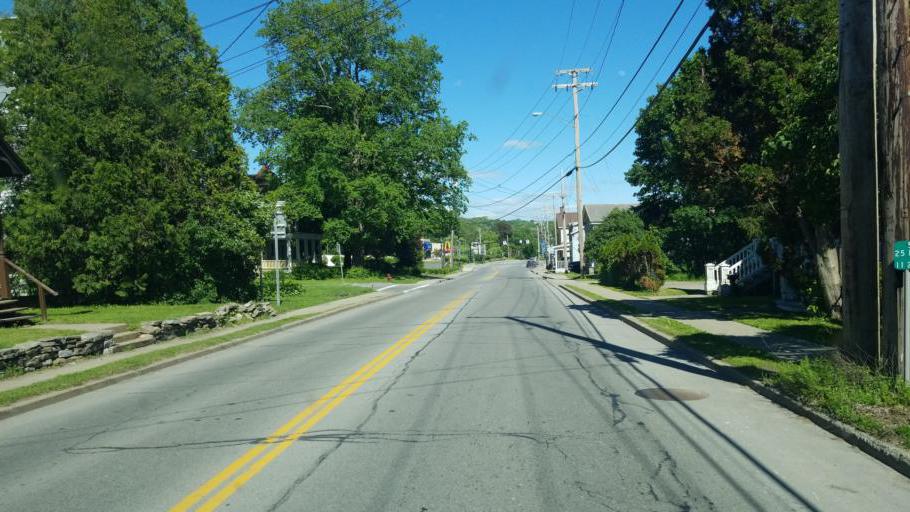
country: US
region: New York
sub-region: Montgomery County
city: Canajoharie
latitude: 42.9111
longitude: -74.5733
